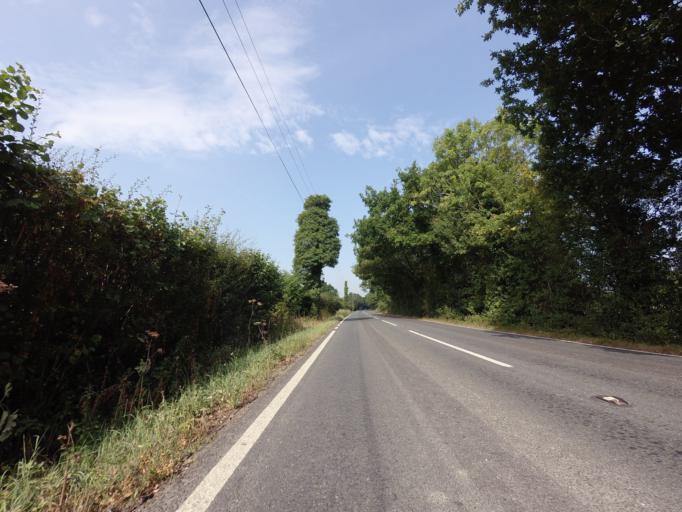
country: GB
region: England
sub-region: Kent
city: Headcorn
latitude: 51.1148
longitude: 0.6265
